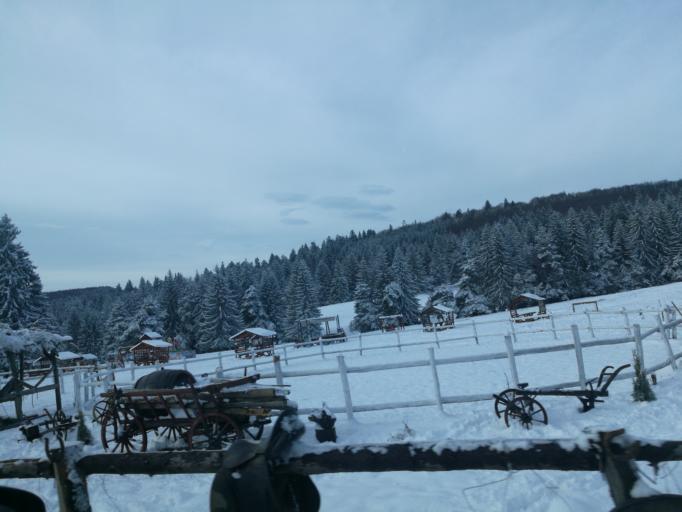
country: RO
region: Brasov
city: Brasov
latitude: 45.6156
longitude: 25.5468
